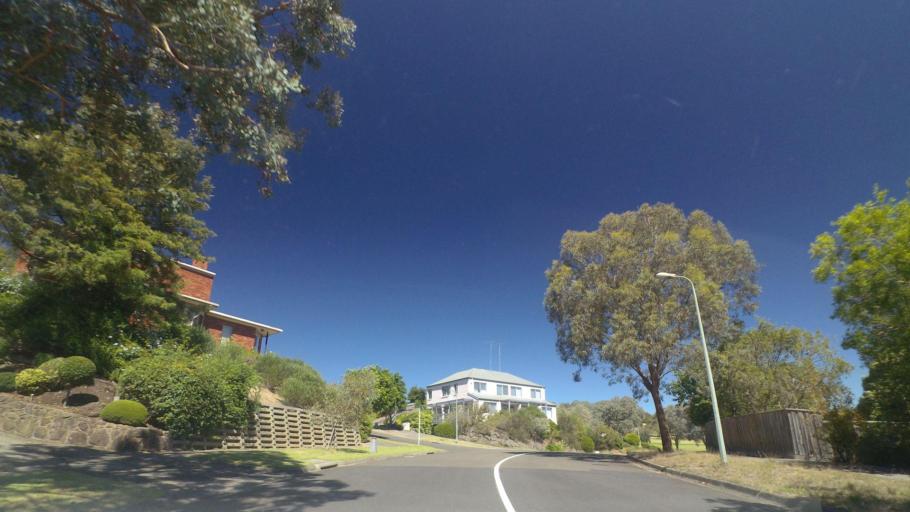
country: AU
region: Victoria
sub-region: Manningham
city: Donvale
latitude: -37.7702
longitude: 145.1753
